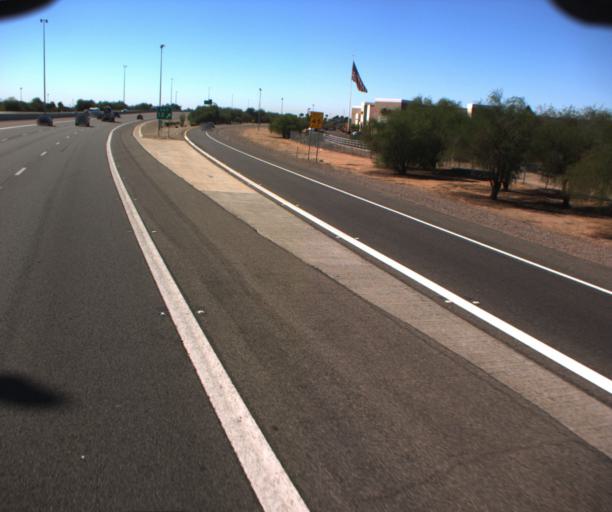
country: US
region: Arizona
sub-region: Maricopa County
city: Peoria
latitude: 33.6144
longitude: -112.2404
